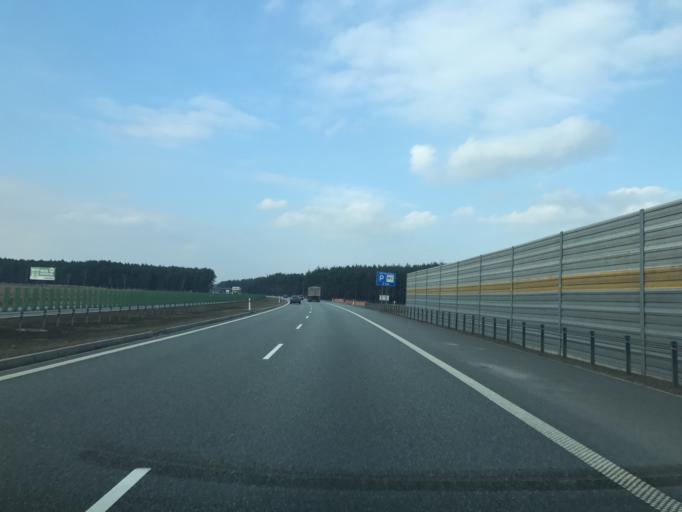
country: PL
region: Kujawsko-Pomorskie
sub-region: Powiat torunski
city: Lubicz Dolny
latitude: 52.9877
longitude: 18.7357
